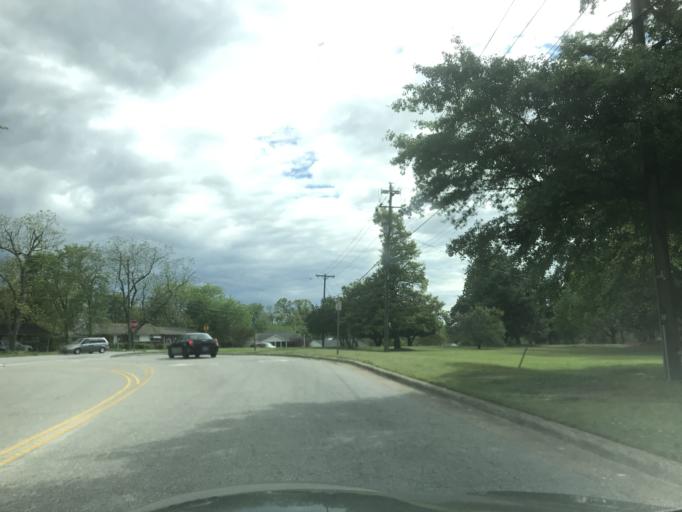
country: US
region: North Carolina
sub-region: Wake County
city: Raleigh
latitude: 35.7724
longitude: -78.5929
